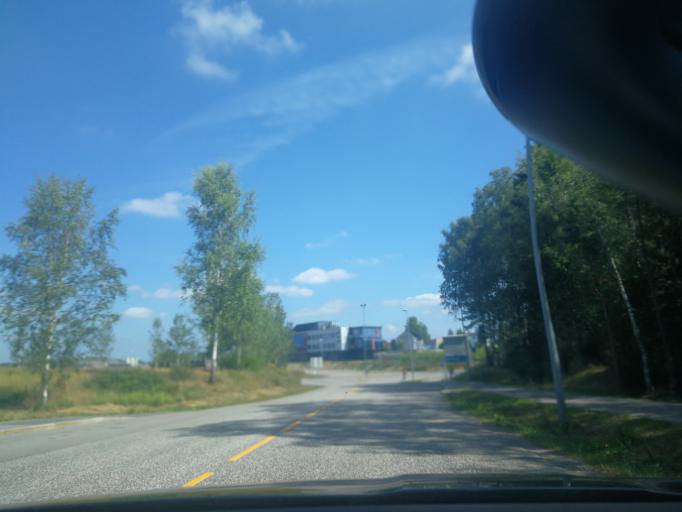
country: NO
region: Vestfold
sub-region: Stokke
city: Stokke
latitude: 59.2072
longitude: 10.2401
